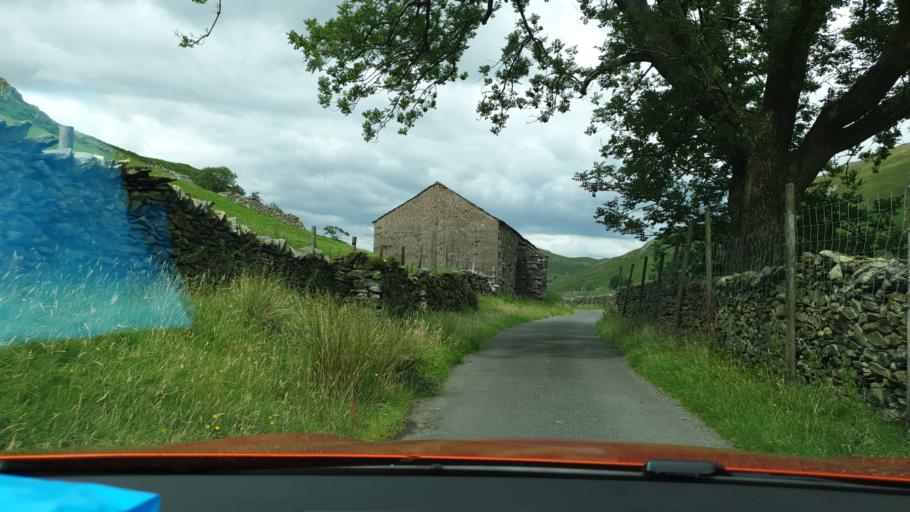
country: GB
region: England
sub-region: Cumbria
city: Ambleside
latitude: 54.5463
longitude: -2.8739
